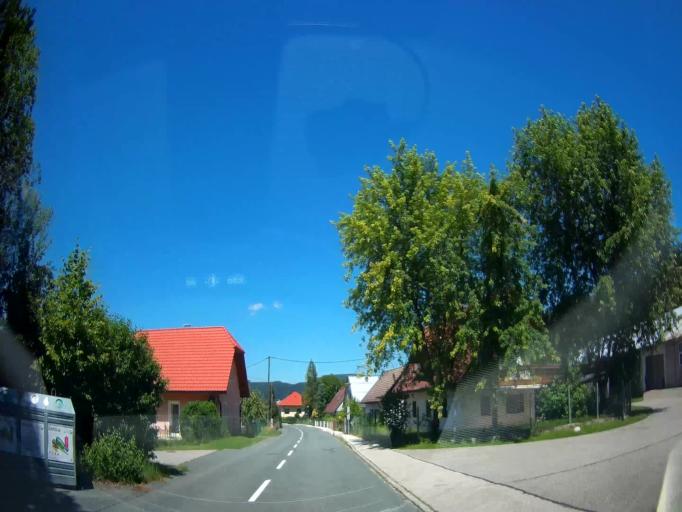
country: AT
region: Carinthia
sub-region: Politischer Bezirk Klagenfurt Land
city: Ferlach
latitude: 46.5188
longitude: 14.2972
